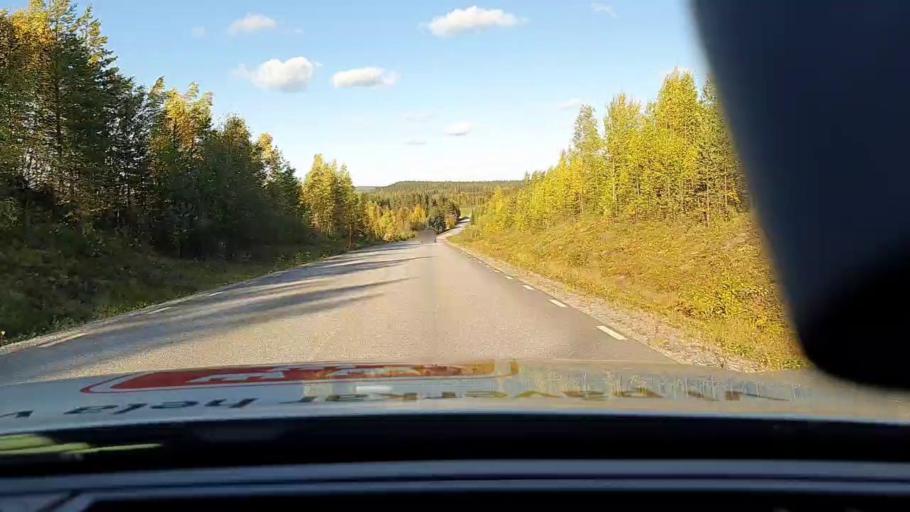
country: SE
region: Norrbotten
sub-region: Pitea Kommun
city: Norrfjarden
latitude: 65.5054
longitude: 21.4804
